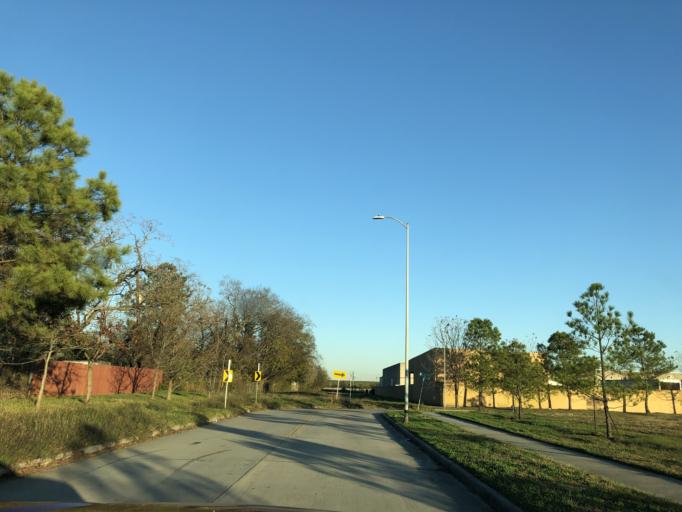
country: US
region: Texas
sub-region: Harris County
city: Jacinto City
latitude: 29.7598
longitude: -95.2692
